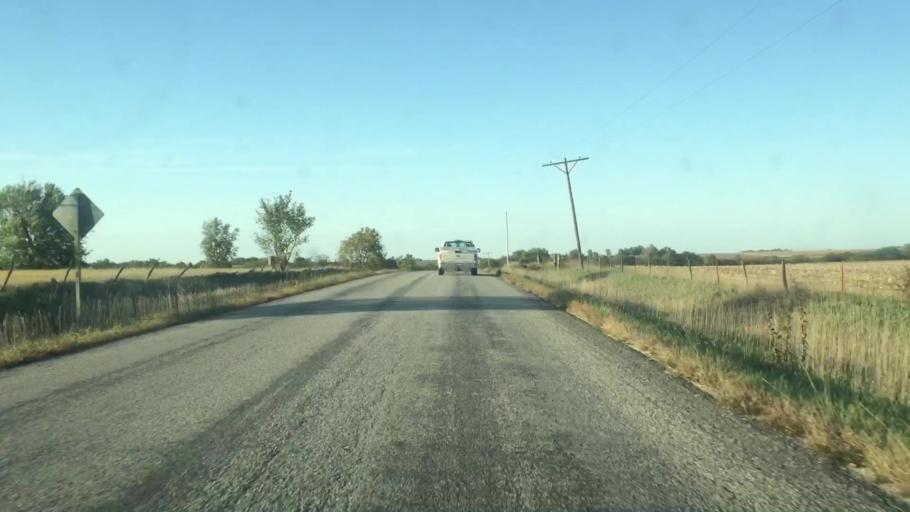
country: US
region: Kansas
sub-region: Brown County
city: Horton
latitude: 39.5524
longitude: -95.4021
